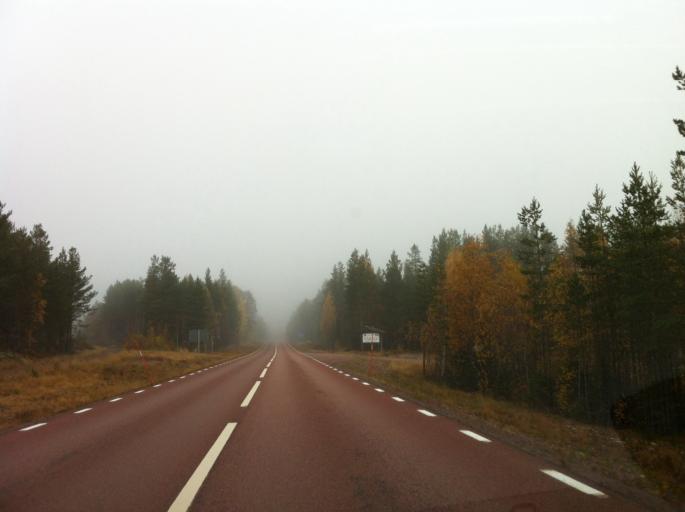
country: NO
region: Hedmark
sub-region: Trysil
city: Innbygda
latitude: 61.6831
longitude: 13.1647
